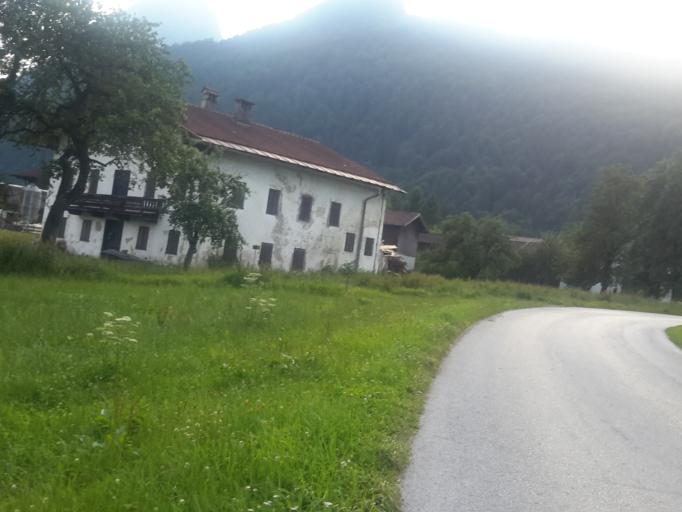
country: AT
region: Tyrol
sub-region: Politischer Bezirk Kufstein
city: Kufstein
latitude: 47.5875
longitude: 12.1560
